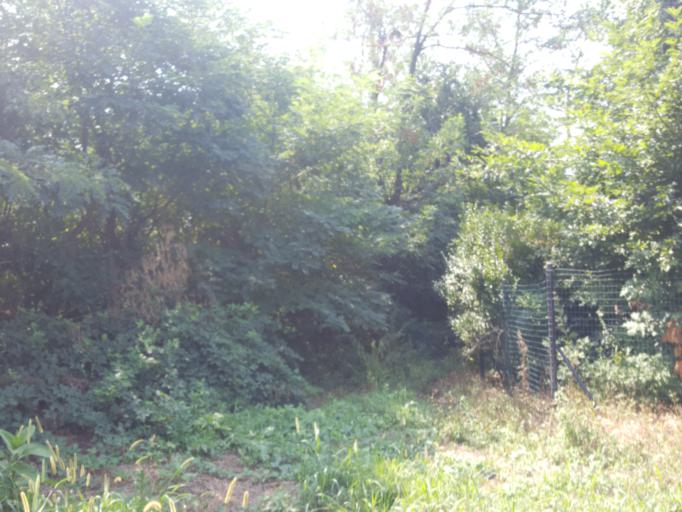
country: IT
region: Lombardy
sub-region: Citta metropolitana di Milano
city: Torrazza dei Mandelli
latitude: 45.5751
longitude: 9.4045
